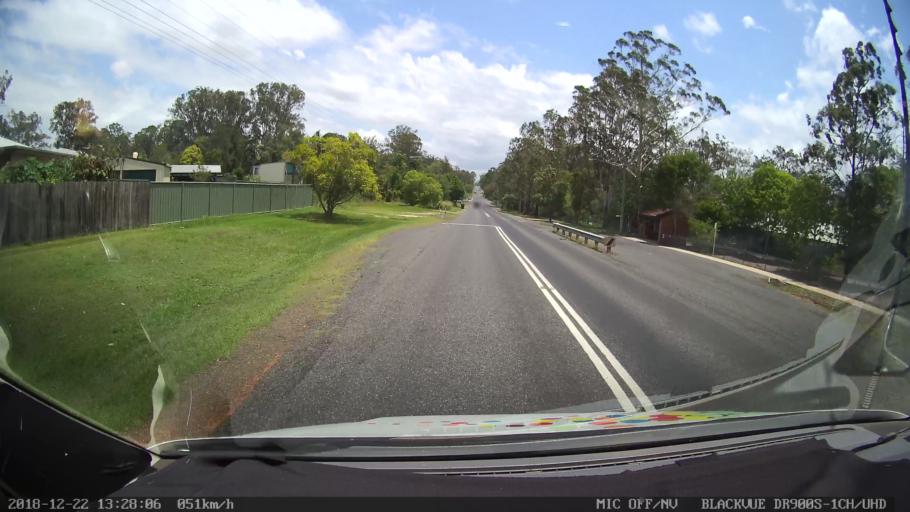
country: AU
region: New South Wales
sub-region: Clarence Valley
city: Coutts Crossing
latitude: -29.8320
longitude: 152.8905
